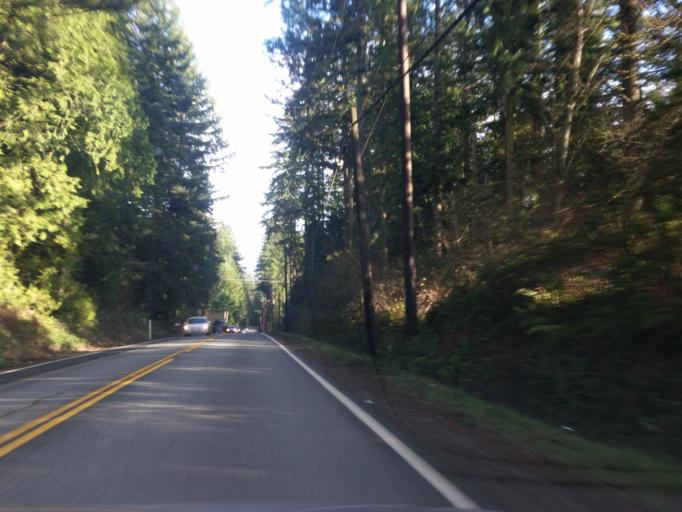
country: US
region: Washington
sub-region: Snohomish County
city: North Creek
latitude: 47.8112
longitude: -122.1738
